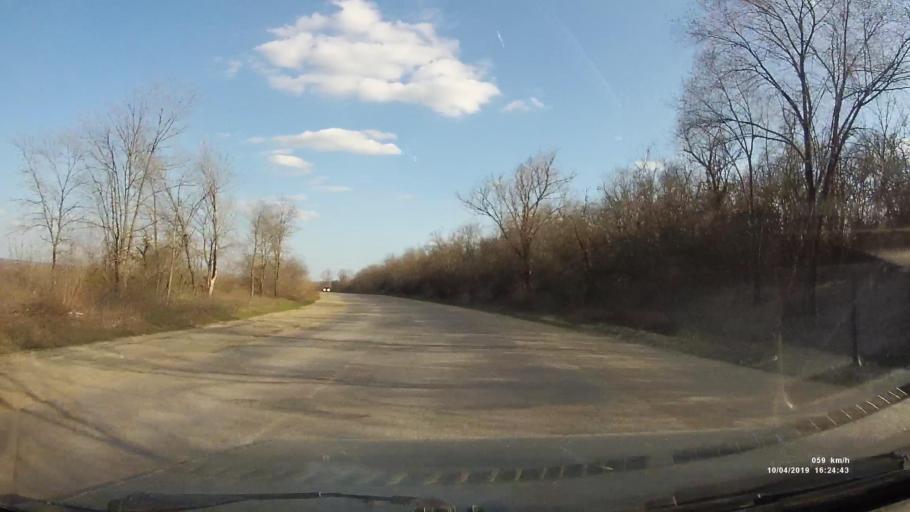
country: RU
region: Rostov
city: Staraya Stanitsa
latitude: 48.2974
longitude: 40.3165
